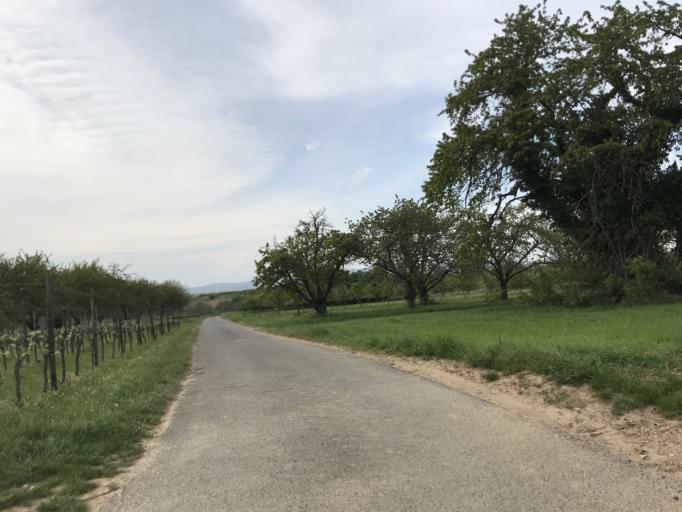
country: DE
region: Rheinland-Pfalz
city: Schwabenheim
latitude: 49.9452
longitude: 8.0962
